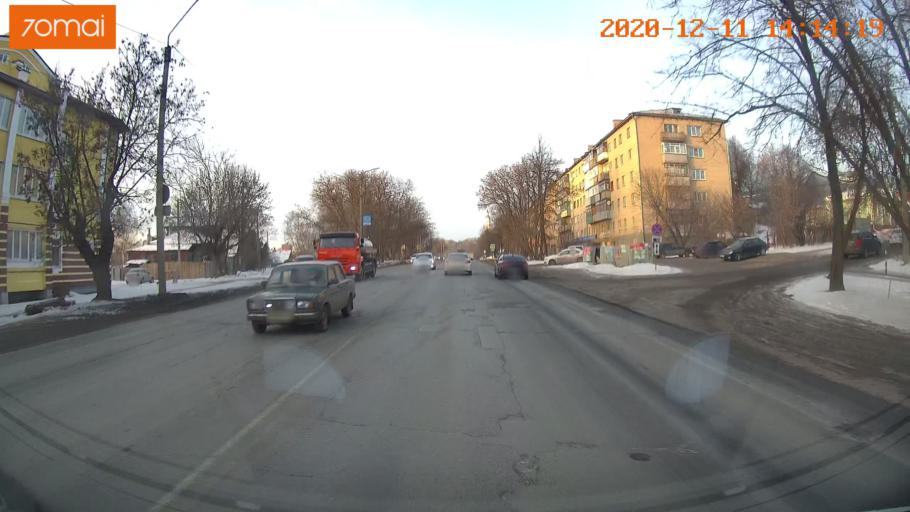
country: RU
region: Kostroma
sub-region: Kostromskoy Rayon
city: Kostroma
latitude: 57.7518
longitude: 40.9524
